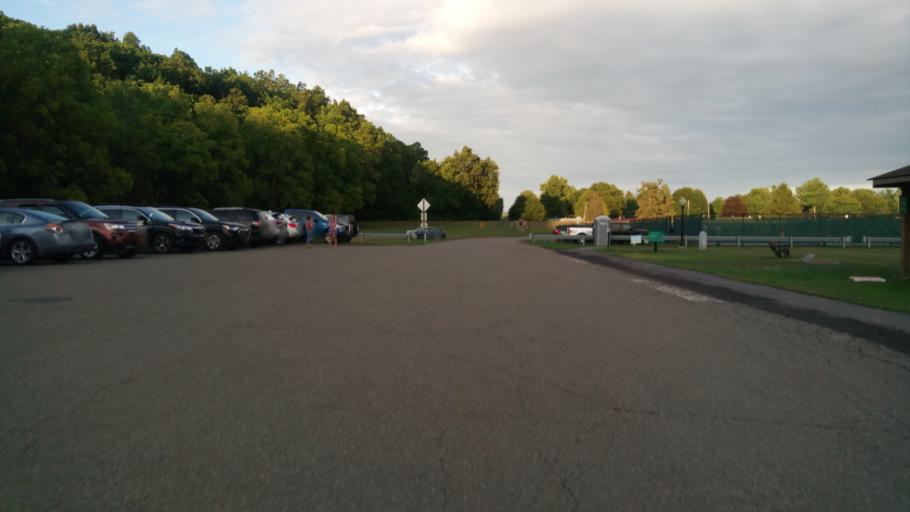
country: US
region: New York
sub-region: Chemung County
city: Southport
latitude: 42.0586
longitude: -76.8279
